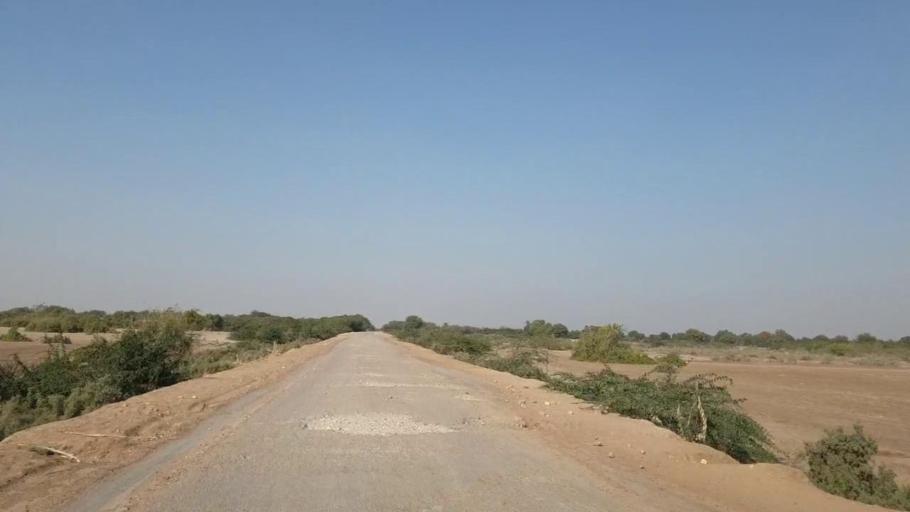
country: PK
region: Sindh
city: Digri
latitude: 24.9895
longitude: 69.1090
